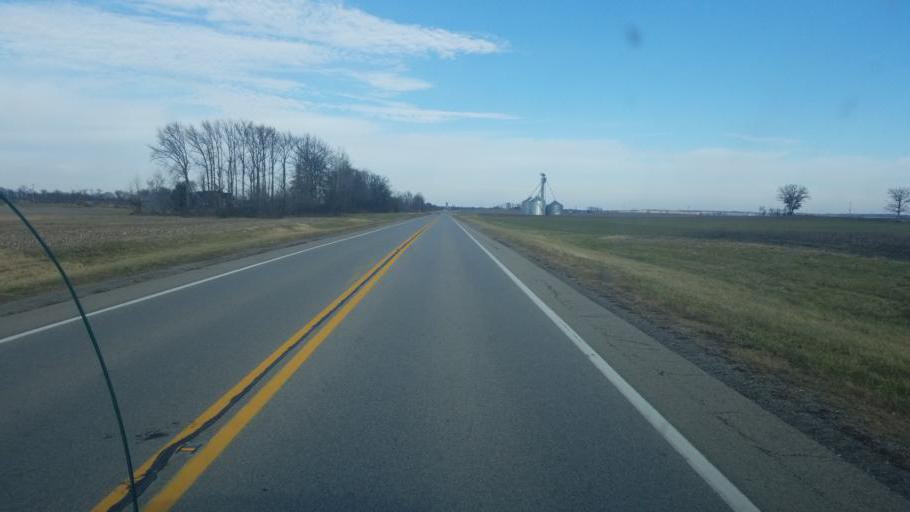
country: US
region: Illinois
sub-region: White County
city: Carmi
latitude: 38.1372
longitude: -88.0925
